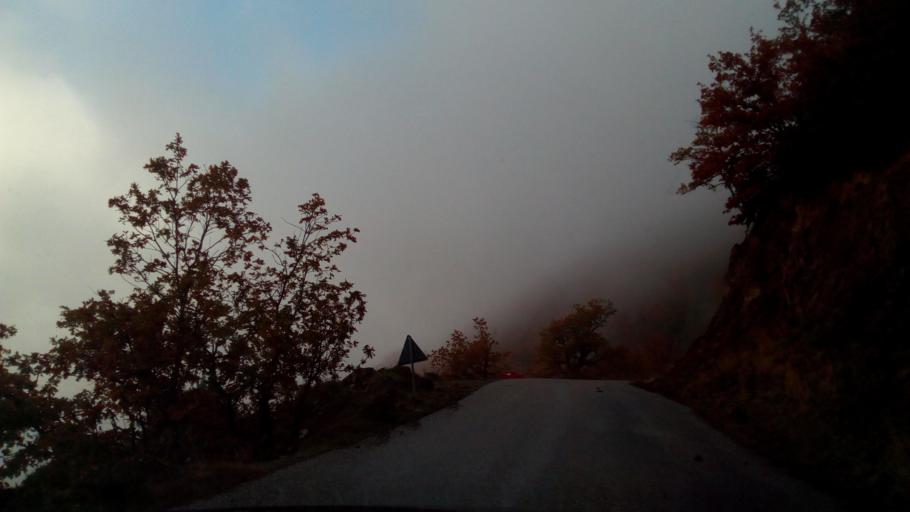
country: GR
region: West Greece
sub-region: Nomos Aitolias kai Akarnanias
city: Nafpaktos
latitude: 38.5533
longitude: 21.9294
